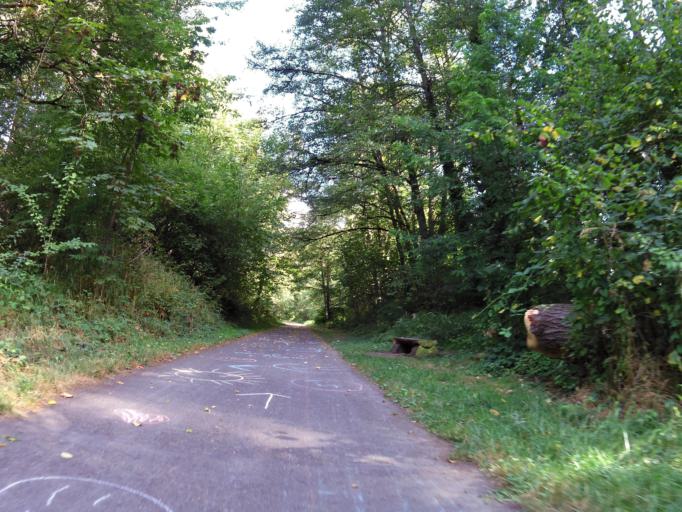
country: US
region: Washington
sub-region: Thurston County
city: Olympia
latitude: 47.0337
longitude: -122.8850
